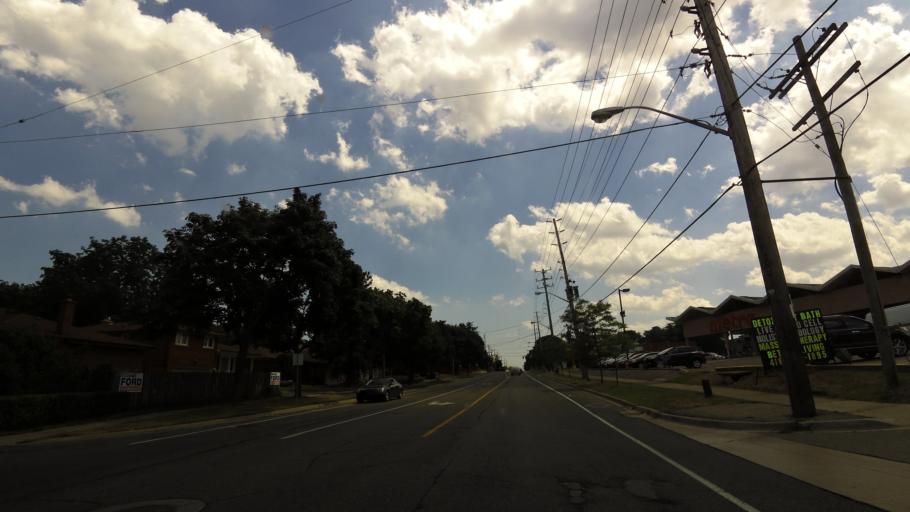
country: CA
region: Ontario
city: Etobicoke
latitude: 43.6920
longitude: -79.5309
